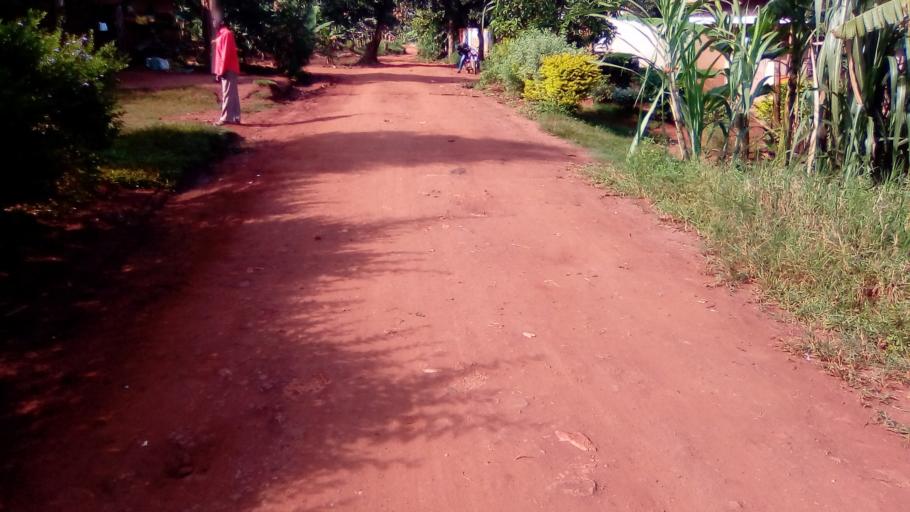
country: UG
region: Central Region
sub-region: Wakiso District
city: Entebbe
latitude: 0.0981
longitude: 32.5272
